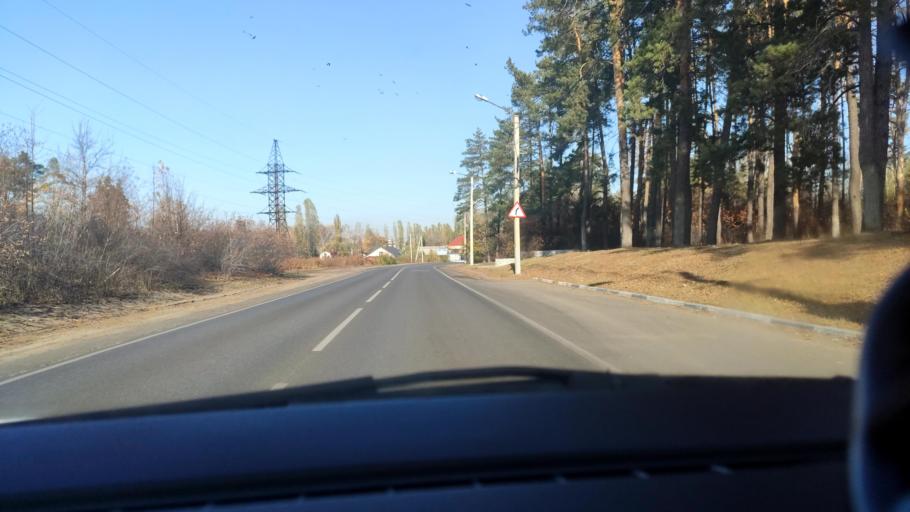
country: RU
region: Voronezj
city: Pridonskoy
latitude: 51.6324
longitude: 39.0824
